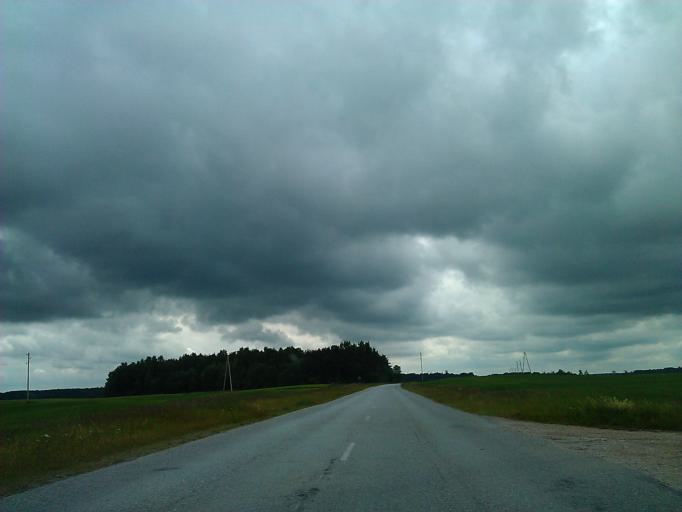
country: LV
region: Aizpute
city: Aizpute
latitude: 56.8275
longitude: 21.7429
